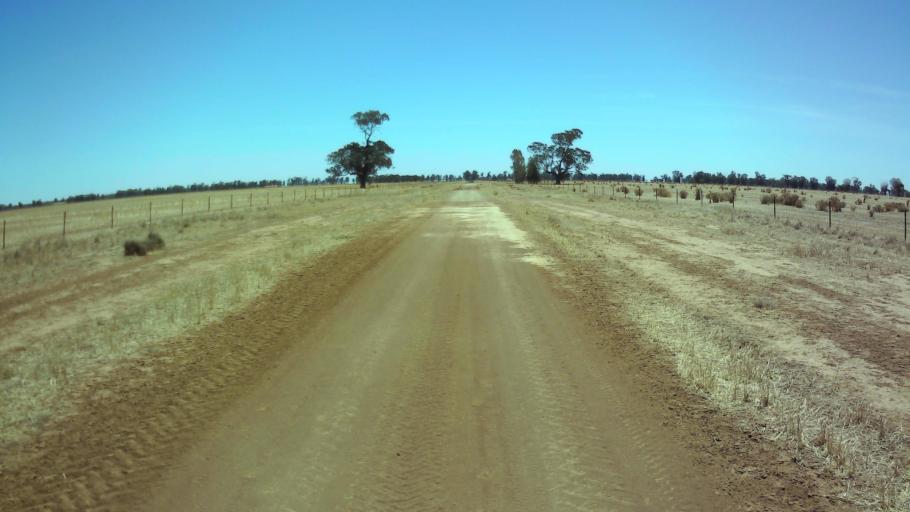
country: AU
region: New South Wales
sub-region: Weddin
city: Grenfell
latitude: -33.9875
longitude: 147.7348
